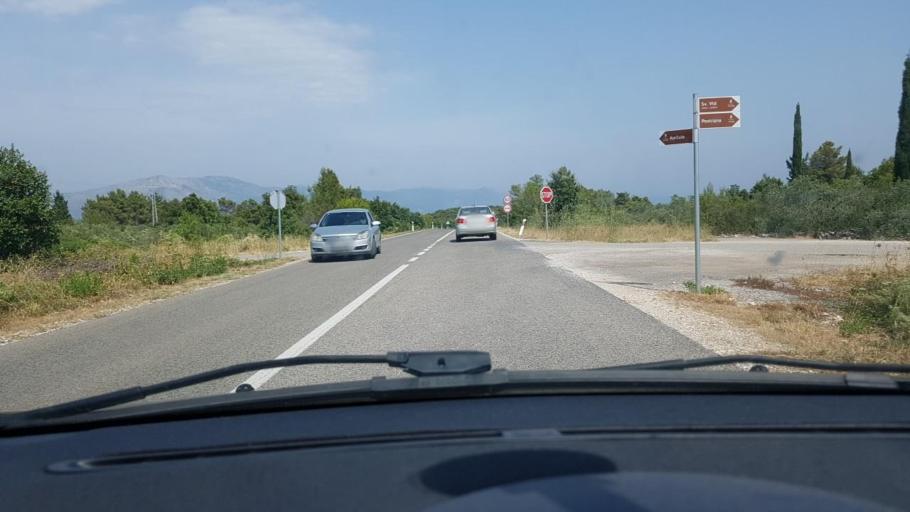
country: HR
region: Dubrovacko-Neretvanska
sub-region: Grad Korcula
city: Zrnovo
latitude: 42.9450
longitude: 17.1158
